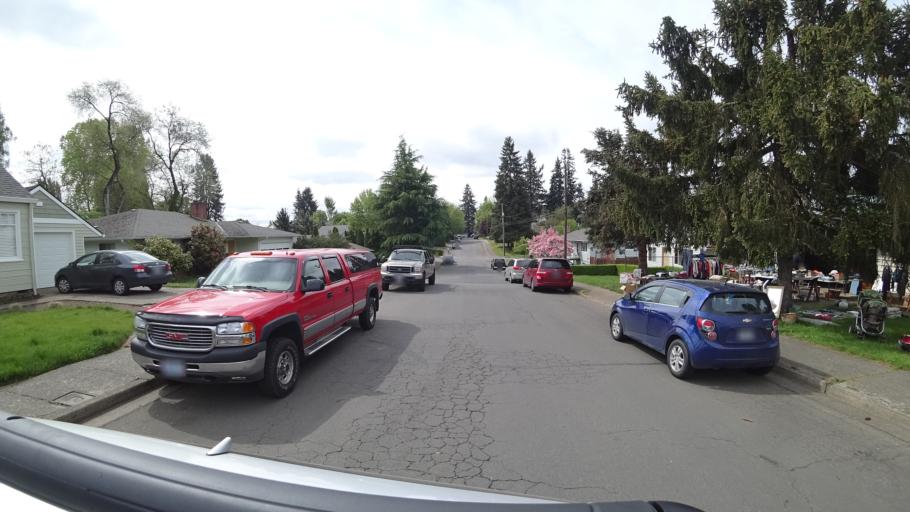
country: US
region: Oregon
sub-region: Washington County
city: Hillsboro
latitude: 45.5247
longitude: -122.9974
